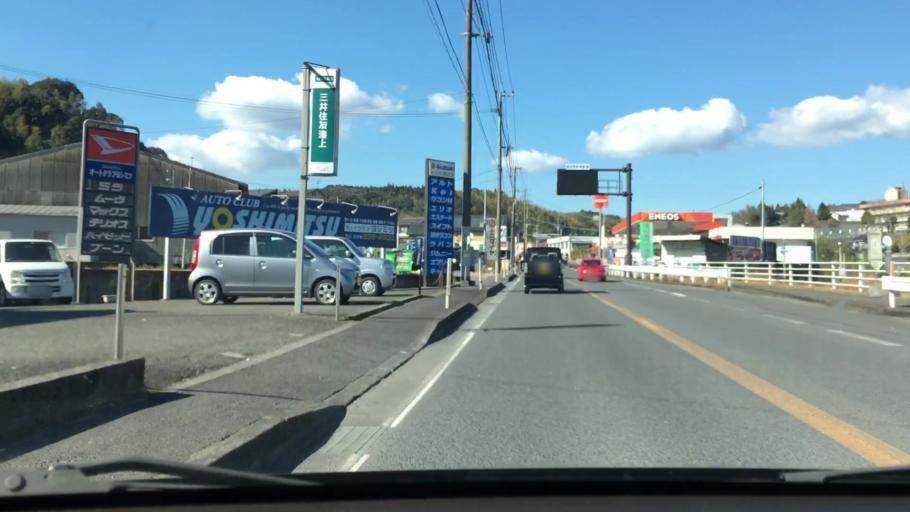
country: JP
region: Kagoshima
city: Ijuin
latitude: 31.6611
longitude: 130.4915
